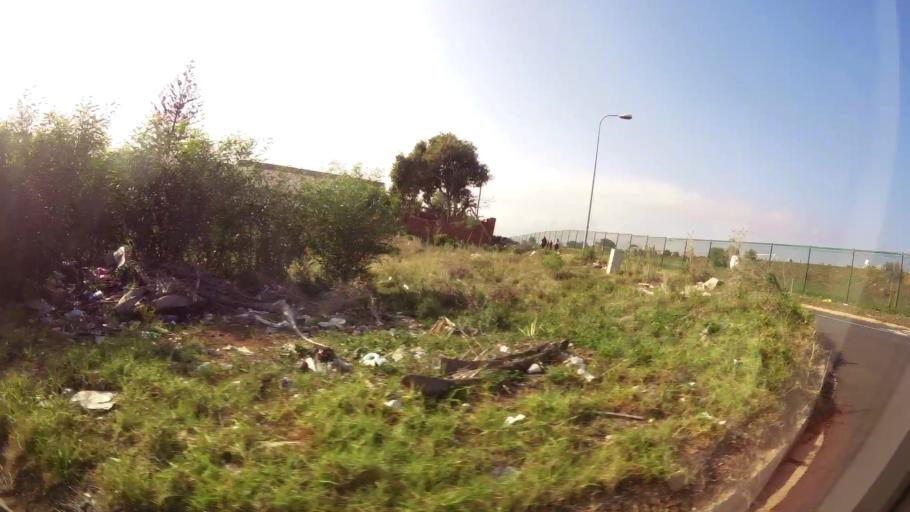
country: ZA
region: Eastern Cape
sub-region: Nelson Mandela Bay Metropolitan Municipality
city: Port Elizabeth
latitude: -33.9264
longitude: 25.5388
